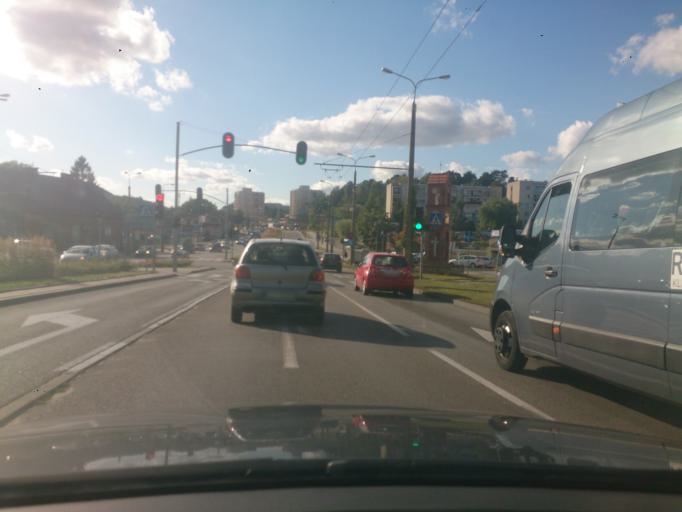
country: PL
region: Pomeranian Voivodeship
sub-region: Gdynia
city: Wielki Kack
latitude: 54.4700
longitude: 18.4975
